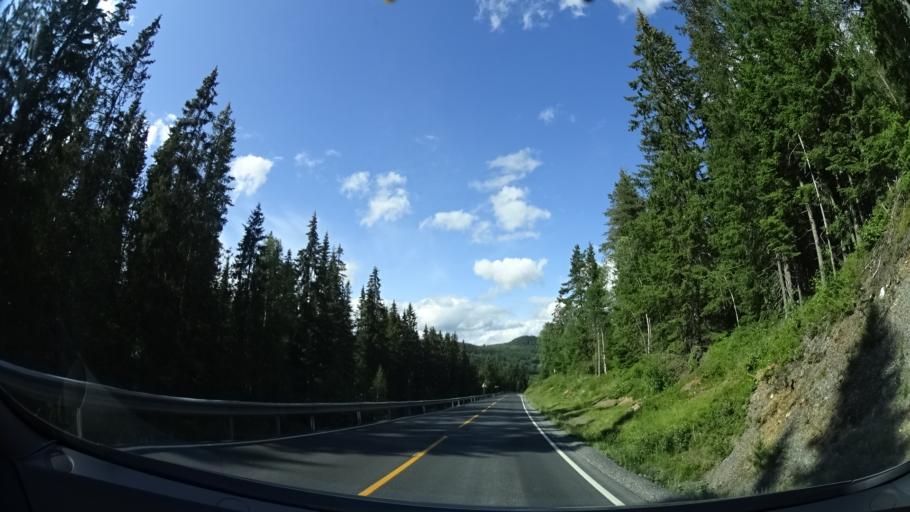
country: NO
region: Sor-Trondelag
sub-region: Snillfjord
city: Krokstadora
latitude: 63.2396
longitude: 9.6047
